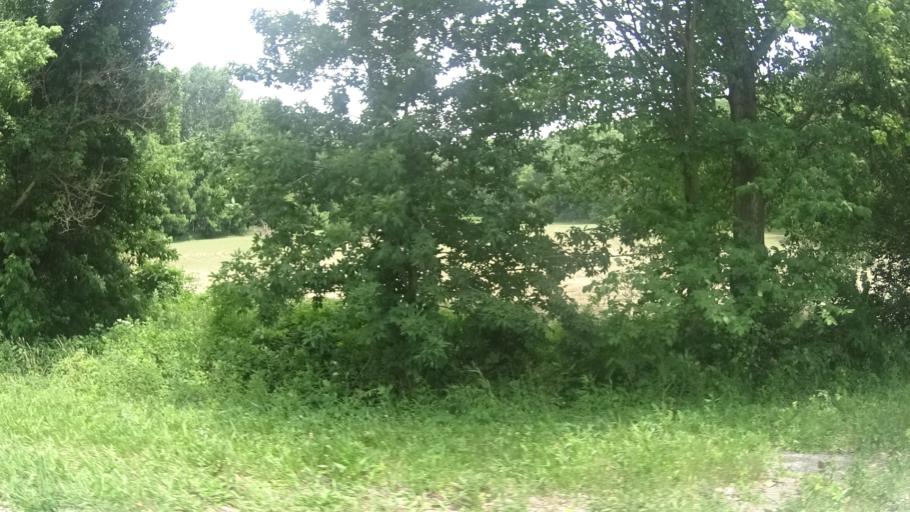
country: US
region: Ohio
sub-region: Erie County
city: Milan
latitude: 41.2857
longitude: -82.6424
